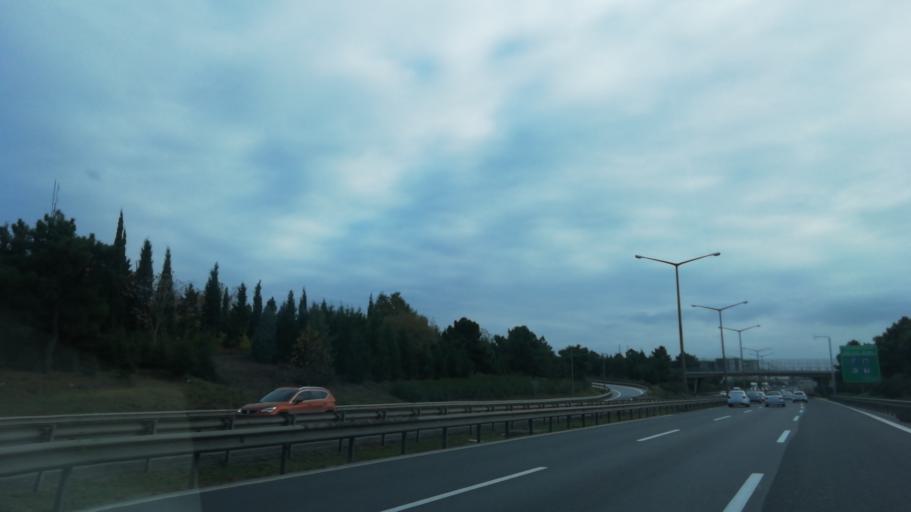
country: TR
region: Kocaeli
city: Korfez
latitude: 40.7704
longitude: 29.7828
